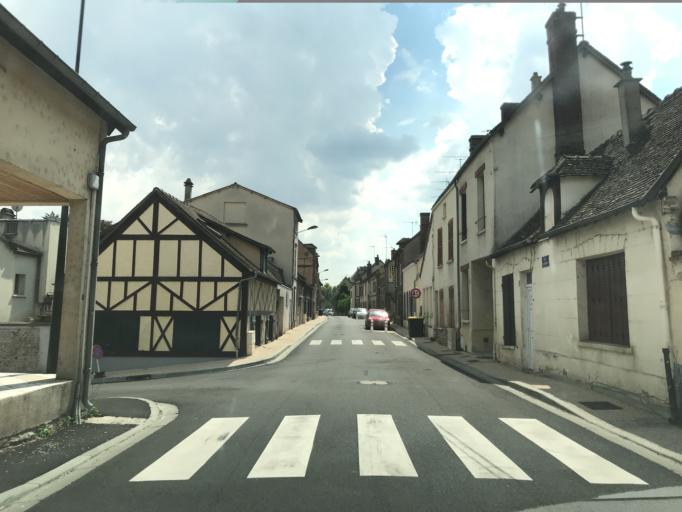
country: FR
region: Haute-Normandie
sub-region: Departement de l'Eure
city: Ivry-la-Bataille
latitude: 48.8857
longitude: 1.4594
